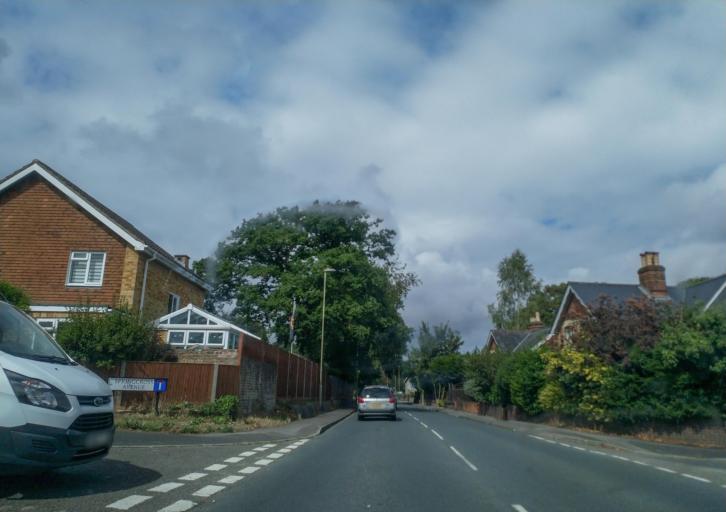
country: GB
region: England
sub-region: Bracknell Forest
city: Sandhurst
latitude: 51.3288
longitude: -0.7847
